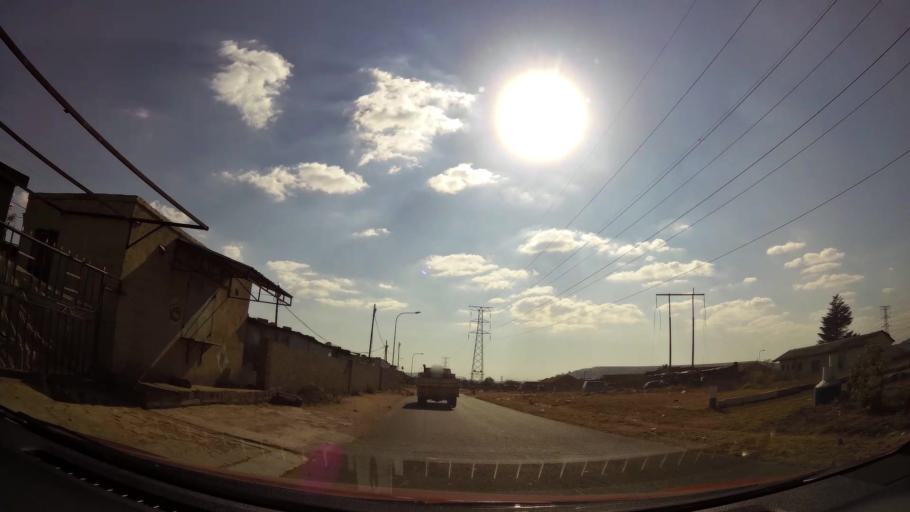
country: ZA
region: Gauteng
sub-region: City of Johannesburg Metropolitan Municipality
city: Soweto
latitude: -26.2384
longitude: 27.9368
